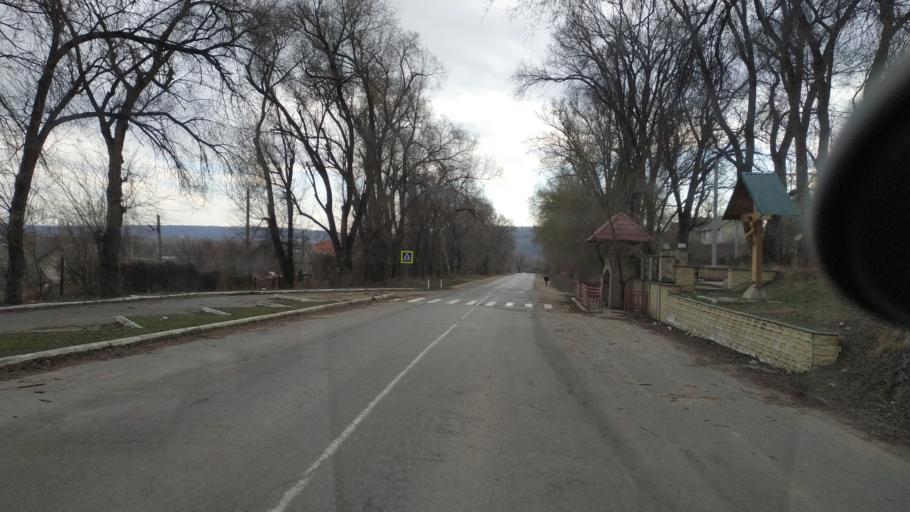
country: MD
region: Chisinau
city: Vadul lui Voda
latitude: 47.1216
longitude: 29.0638
